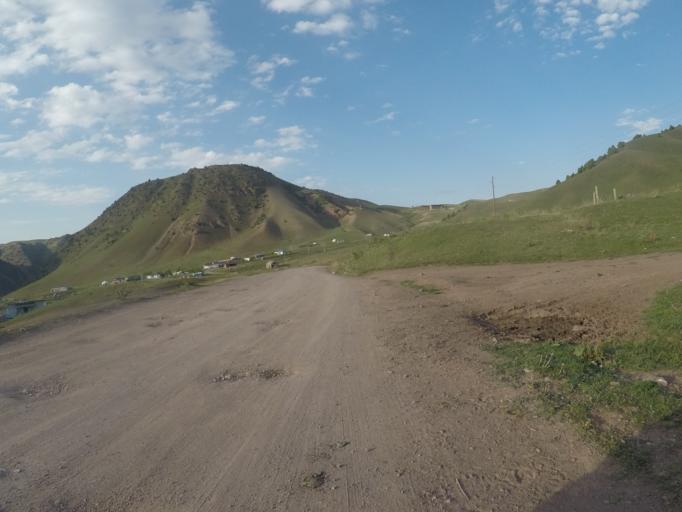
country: KG
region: Chuy
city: Bishkek
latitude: 42.6375
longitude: 74.6190
